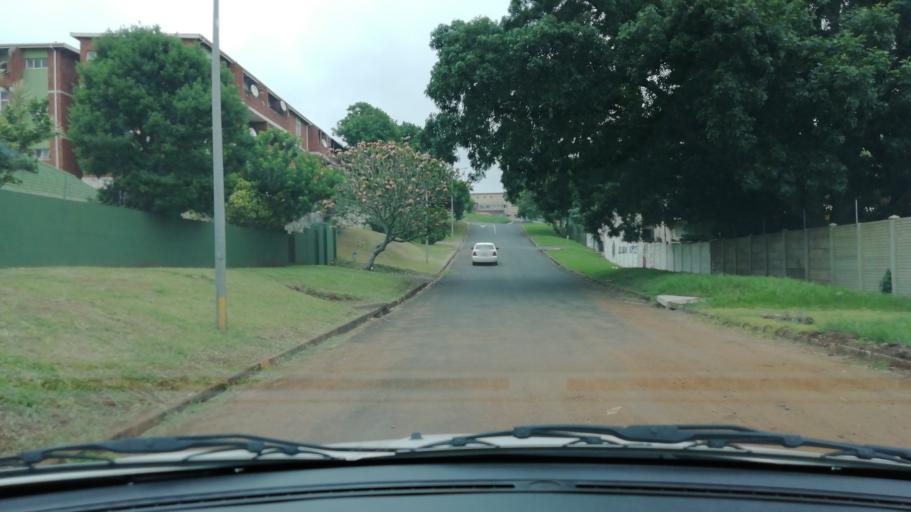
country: ZA
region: KwaZulu-Natal
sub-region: uThungulu District Municipality
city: Empangeni
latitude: -28.7432
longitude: 31.8949
